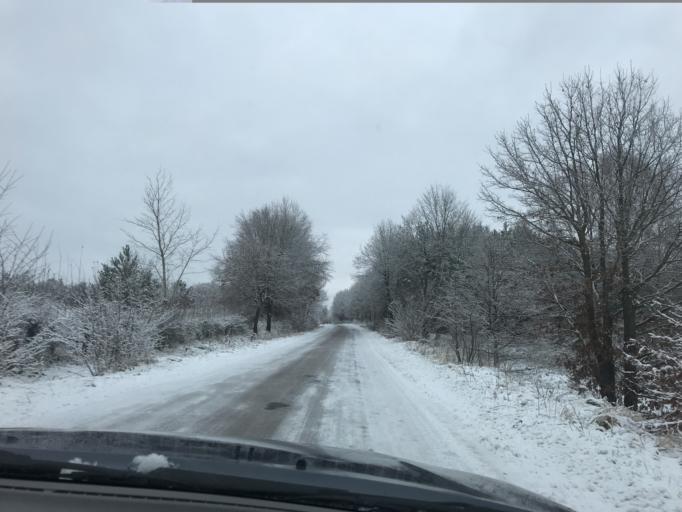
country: PL
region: Pomeranian Voivodeship
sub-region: Powiat bytowski
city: Parchowo
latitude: 54.2318
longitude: 17.5723
